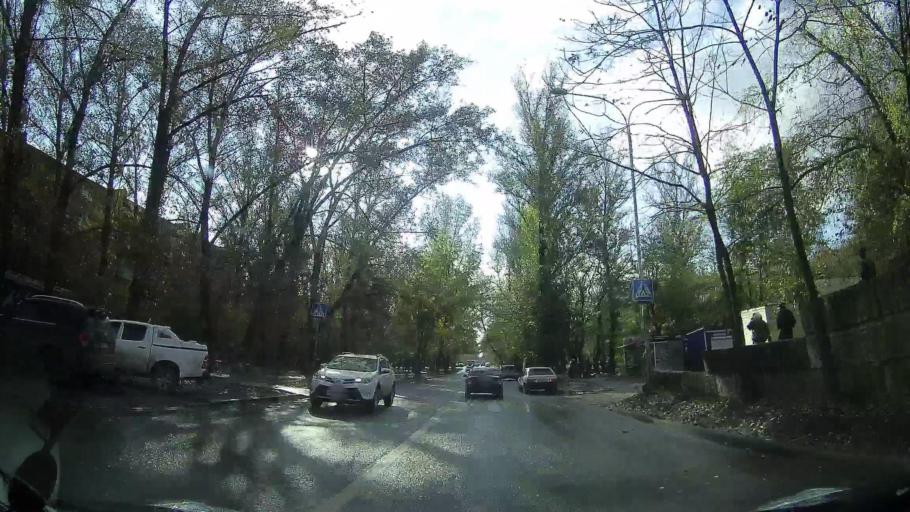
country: RU
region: Rostov
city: Severnyy
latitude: 47.2659
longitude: 39.6660
